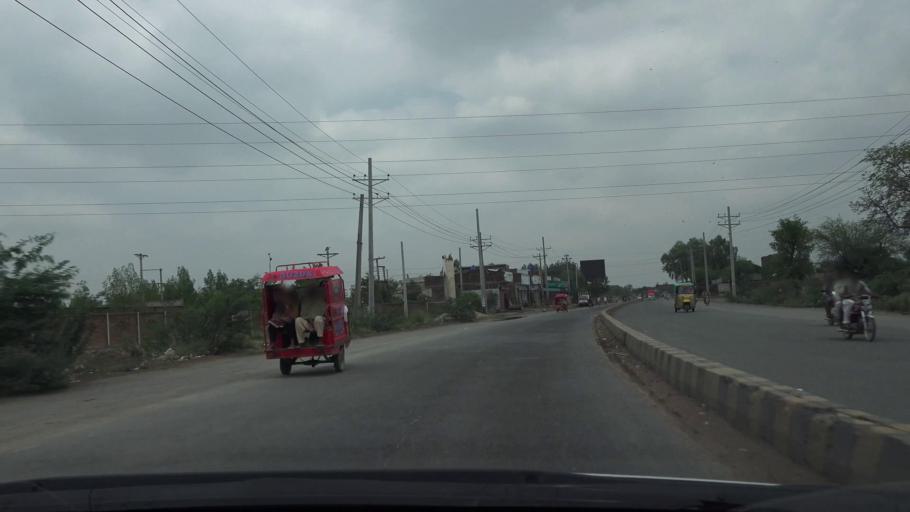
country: PK
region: Punjab
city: Faisalabad
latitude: 31.3917
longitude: 73.1880
